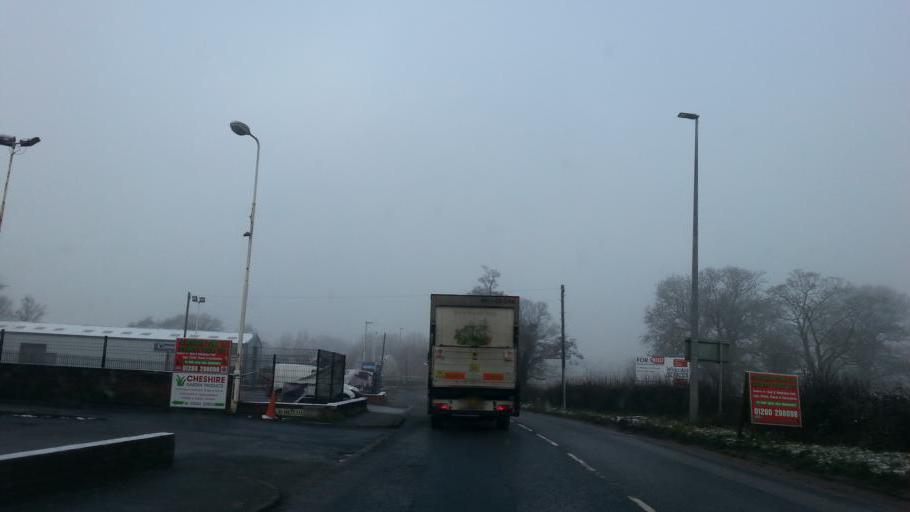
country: GB
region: England
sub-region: Cheshire East
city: Eaton
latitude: 53.1772
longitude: -2.2094
